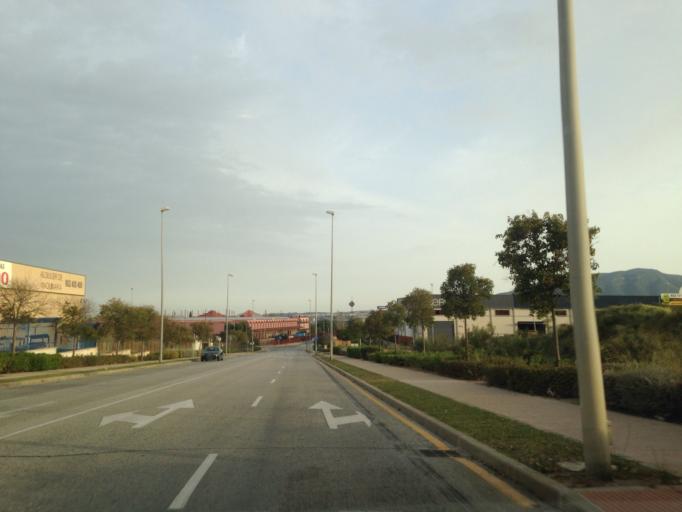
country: ES
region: Andalusia
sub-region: Provincia de Malaga
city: Alhaurin de la Torre
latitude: 36.7171
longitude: -4.5176
